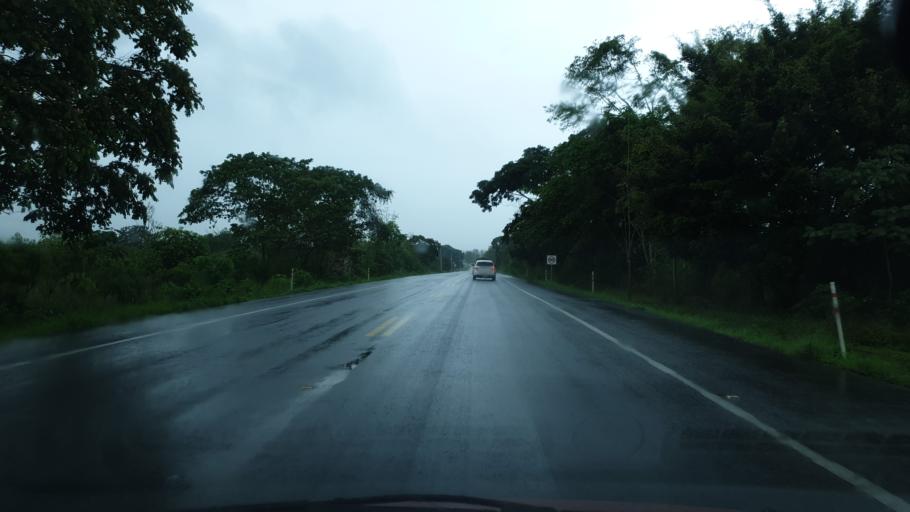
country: EC
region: Manabi
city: Pajan
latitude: -1.7052
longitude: -80.4214
